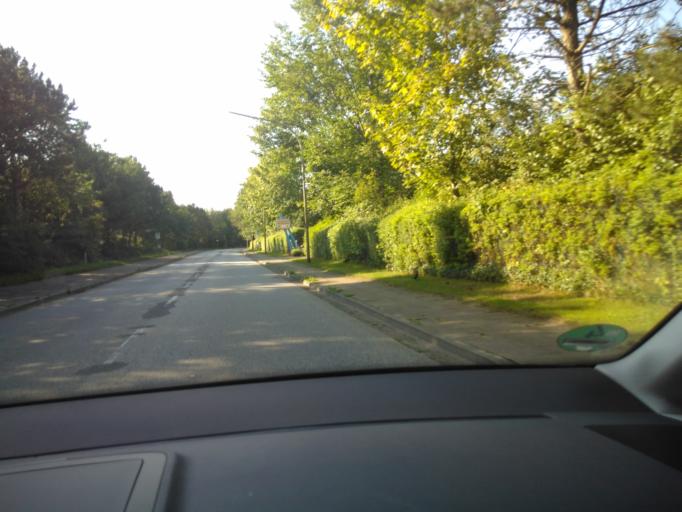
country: DE
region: Lower Saxony
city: Cuxhaven
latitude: 53.8775
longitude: 8.6516
